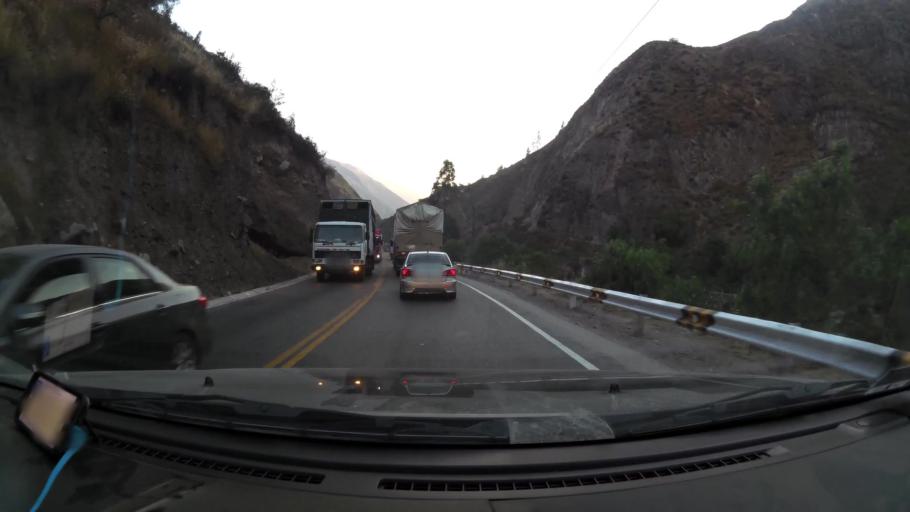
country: PE
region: Lima
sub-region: Provincia de Huarochiri
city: Matucana
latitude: -11.8182
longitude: -76.3599
